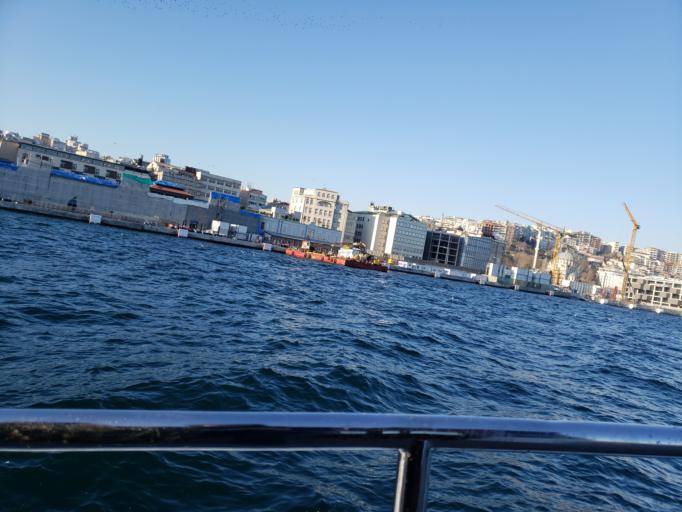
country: TR
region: Istanbul
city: Eminoenue
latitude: 41.0231
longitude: 28.9816
